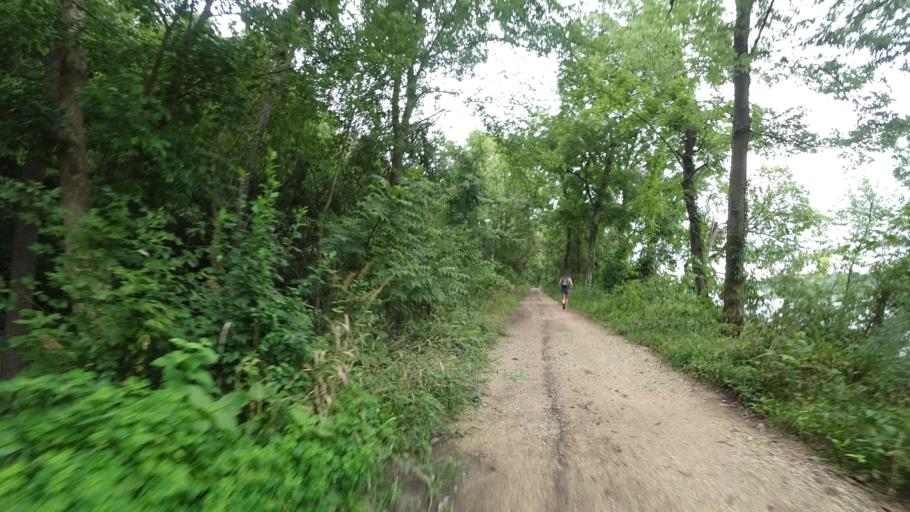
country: US
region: Virginia
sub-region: Loudoun County
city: Lowes Island
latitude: 39.0681
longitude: -77.3528
